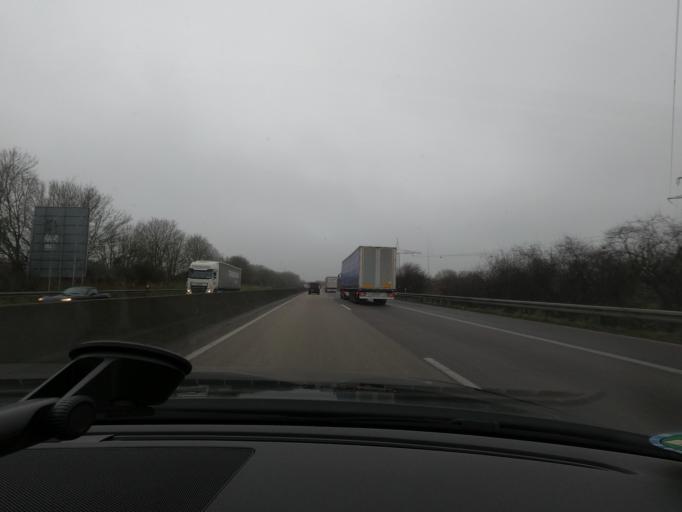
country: DE
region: North Rhine-Westphalia
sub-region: Regierungsbezirk Koln
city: Elsdorf
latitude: 50.9508
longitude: 6.5955
